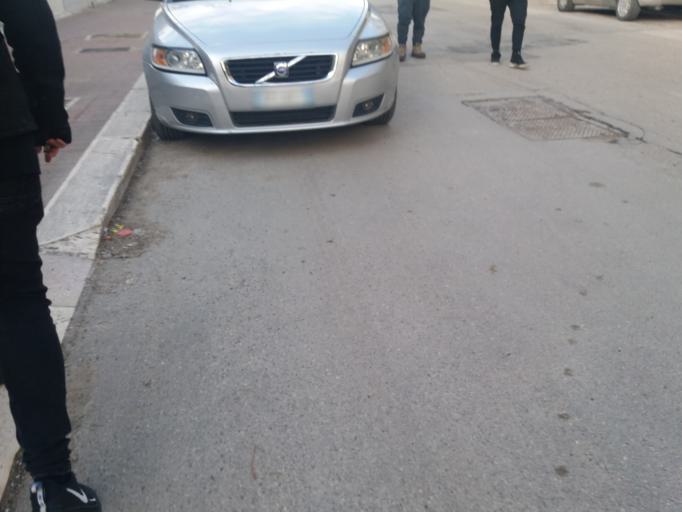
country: IT
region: Apulia
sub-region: Provincia di Barletta - Andria - Trani
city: Andria
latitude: 41.2380
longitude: 16.2920
